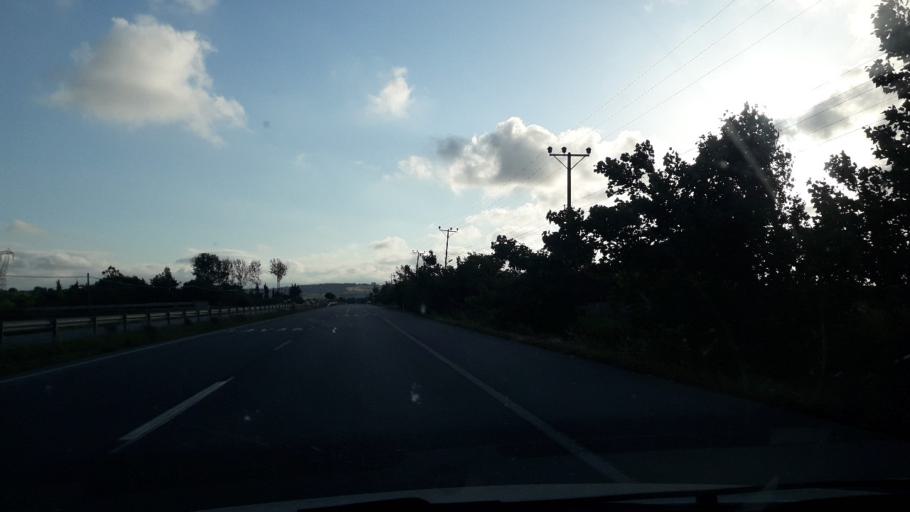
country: TR
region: Samsun
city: Bafra
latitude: 41.6018
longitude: 35.7957
